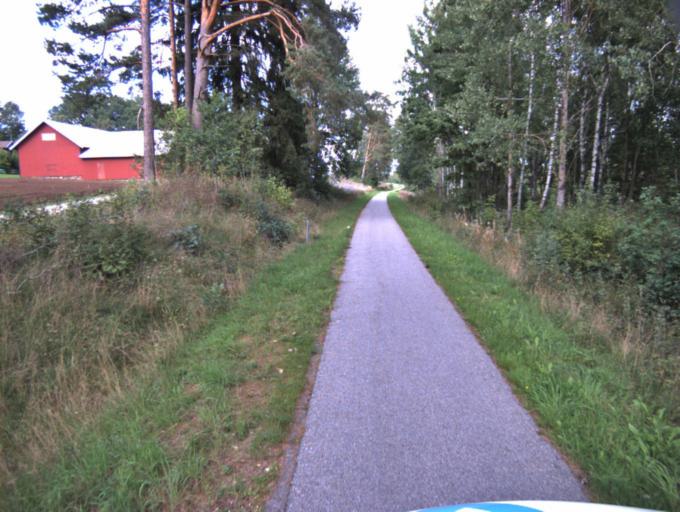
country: SE
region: Vaestra Goetaland
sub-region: Ulricehamns Kommun
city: Ulricehamn
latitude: 57.8444
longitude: 13.4221
